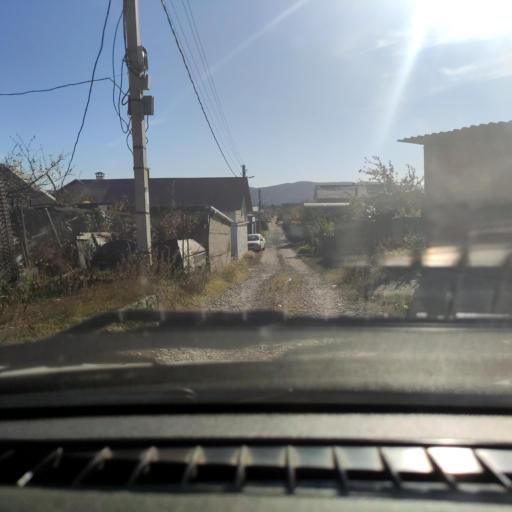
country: RU
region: Samara
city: Zhigulevsk
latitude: 53.4683
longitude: 49.5868
